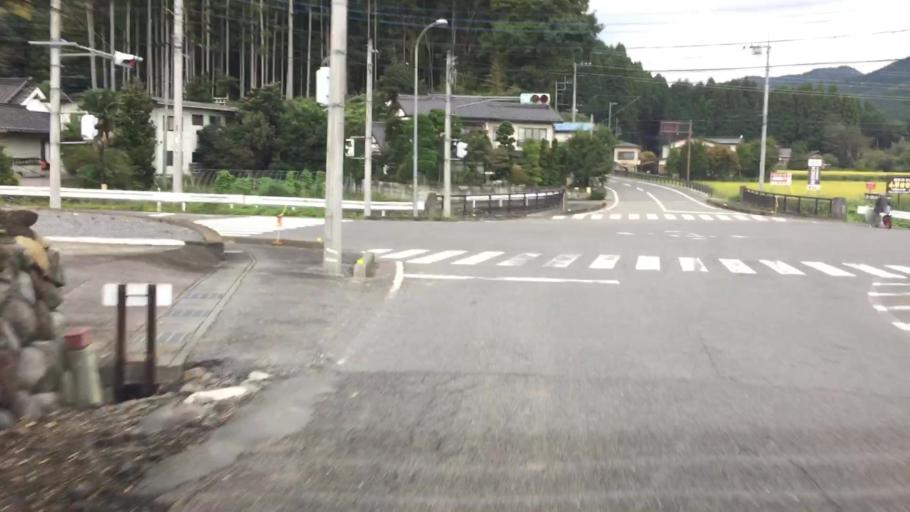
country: JP
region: Tochigi
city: Imaichi
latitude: 36.7647
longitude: 139.6758
